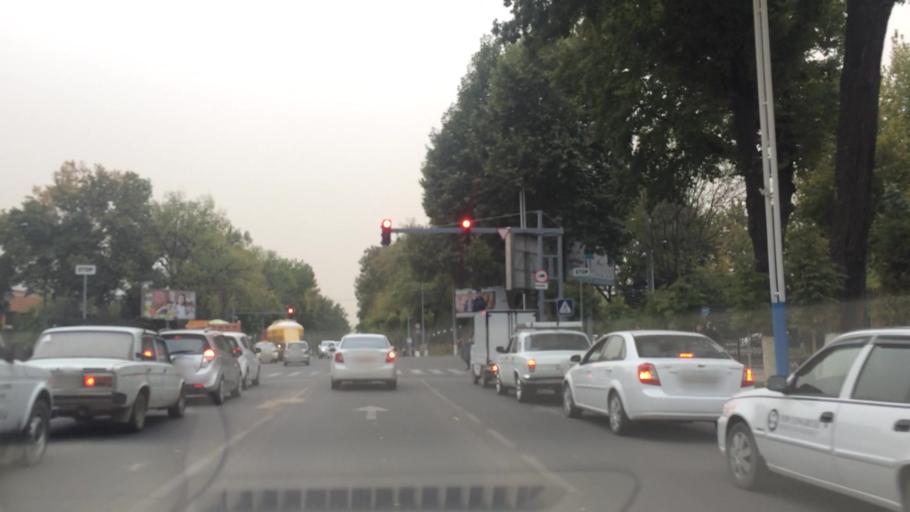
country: UZ
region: Toshkent Shahri
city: Tashkent
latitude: 41.3092
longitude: 69.2873
